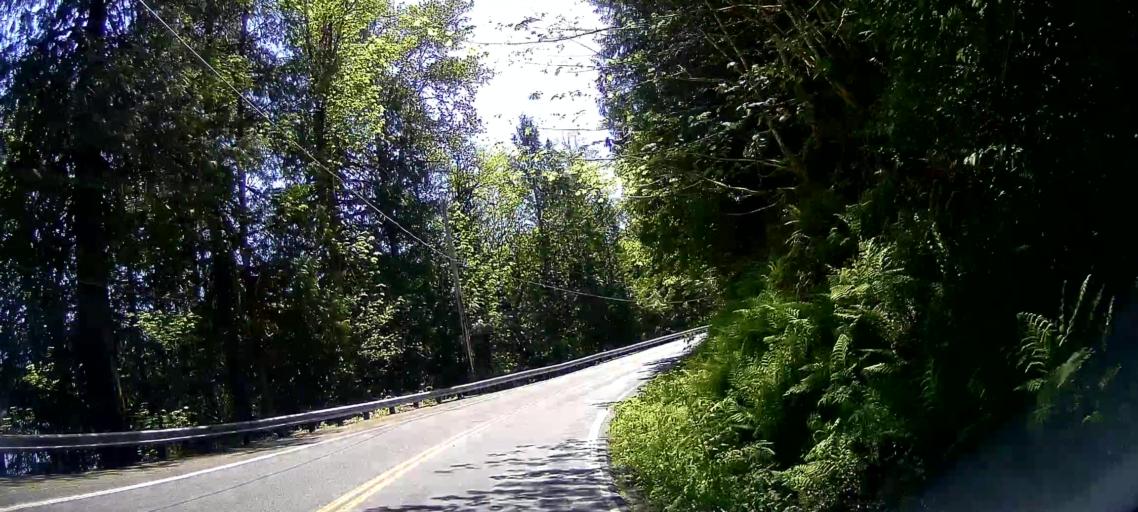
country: US
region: Washington
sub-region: Snohomish County
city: Darrington
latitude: 48.4779
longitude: -121.6479
